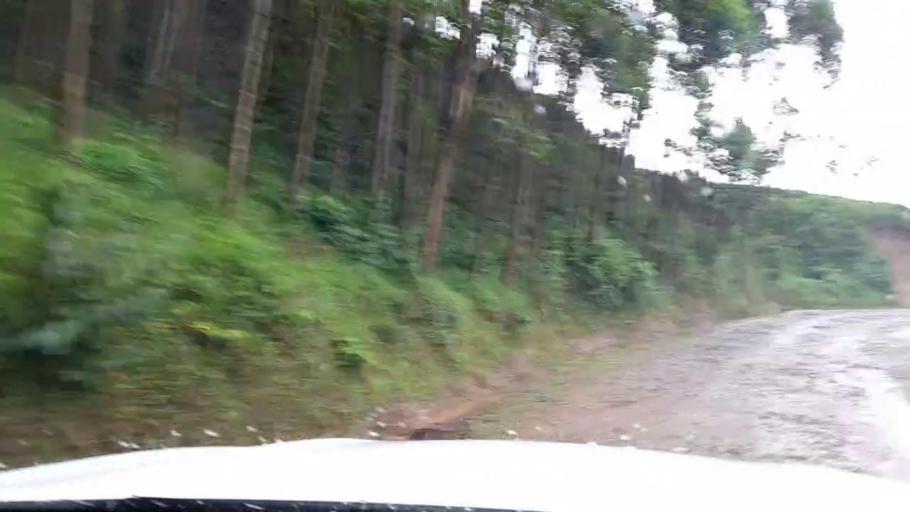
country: RW
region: Western Province
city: Cyangugu
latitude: -2.4578
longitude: 29.0370
